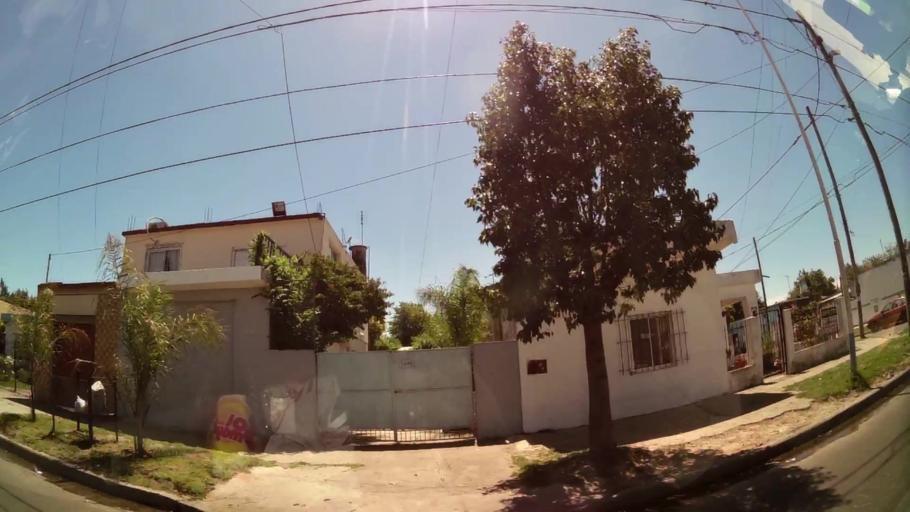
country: AR
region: Buenos Aires
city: Hurlingham
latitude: -34.4906
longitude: -58.6672
